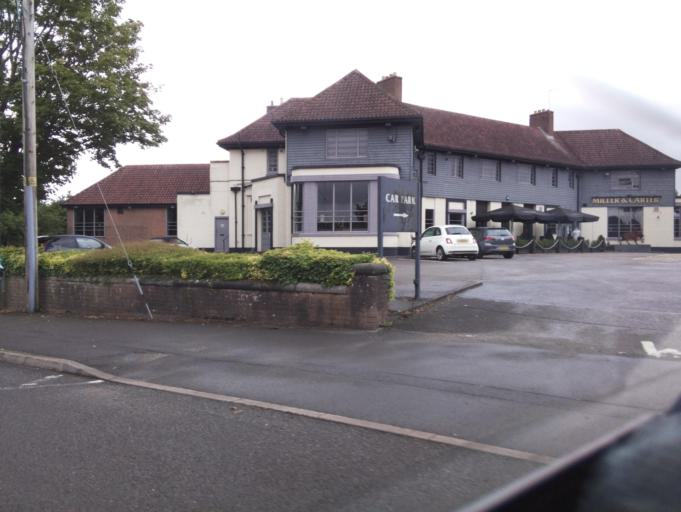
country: GB
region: England
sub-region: Solihull
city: Dickens Heath
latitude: 52.3916
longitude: -1.8255
